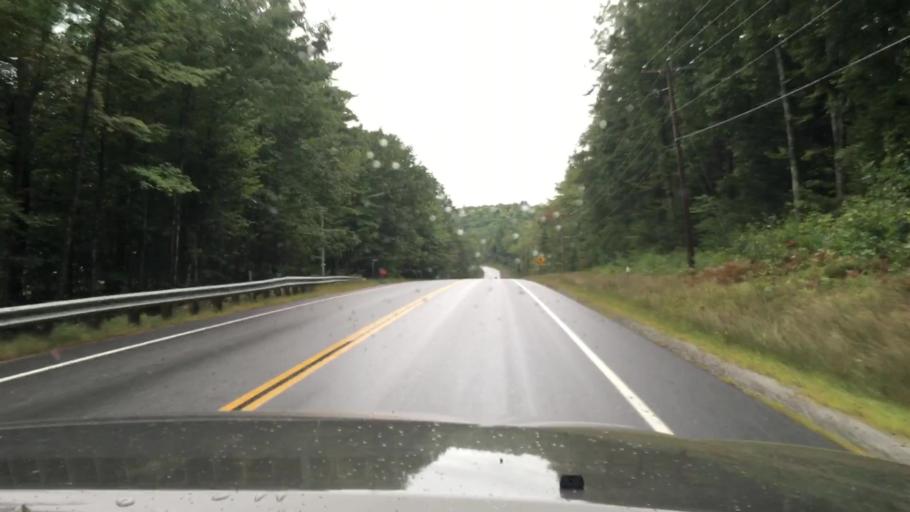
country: US
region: New Hampshire
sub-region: Hillsborough County
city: Hillsborough
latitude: 43.0992
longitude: -71.9610
